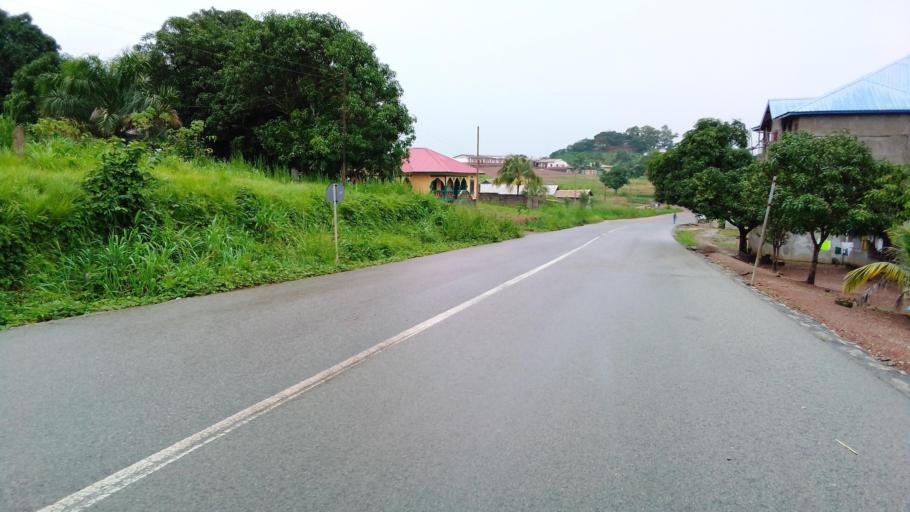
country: SL
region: Eastern Province
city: Kenema
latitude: 7.8773
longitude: -11.1681
